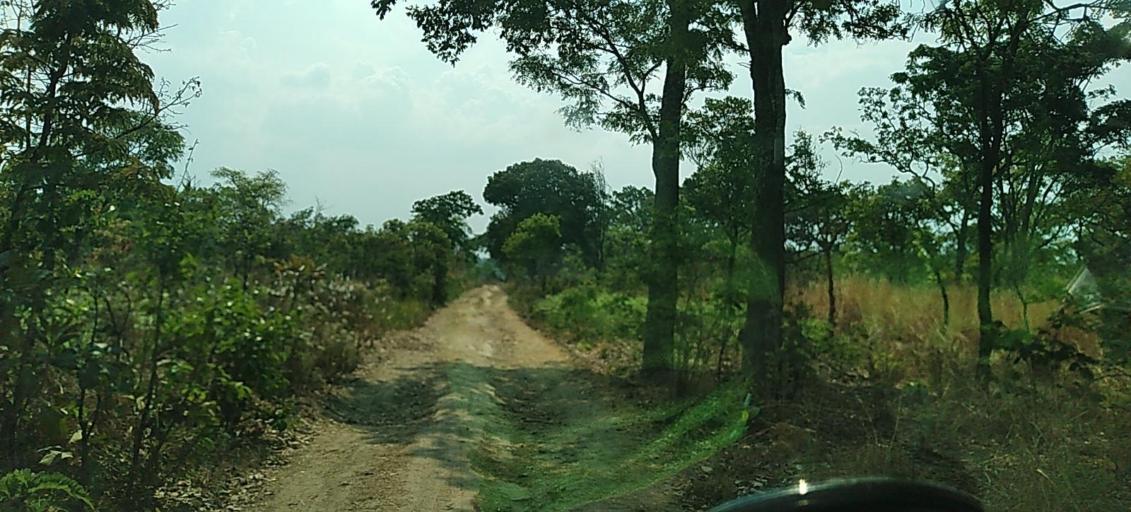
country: ZM
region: North-Western
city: Solwezi
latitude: -12.0932
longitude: 26.2869
